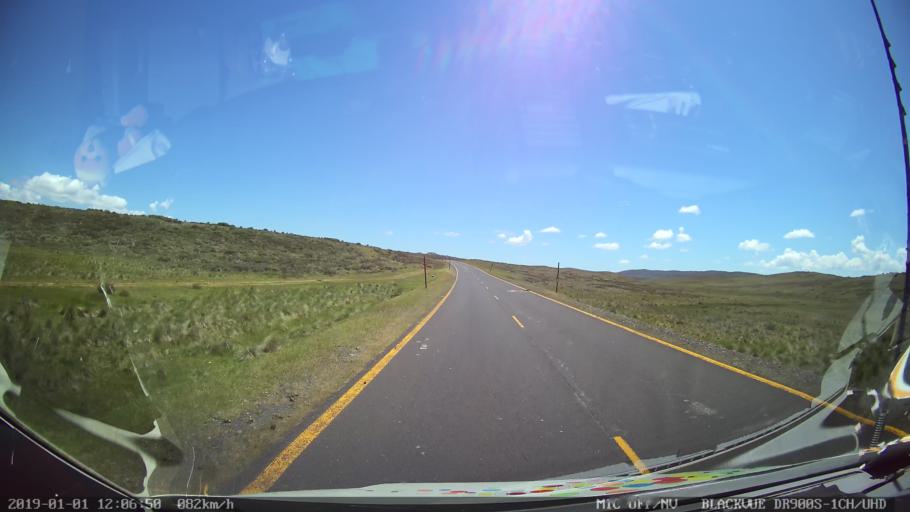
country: AU
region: New South Wales
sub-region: Snowy River
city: Jindabyne
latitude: -35.8404
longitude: 148.4911
